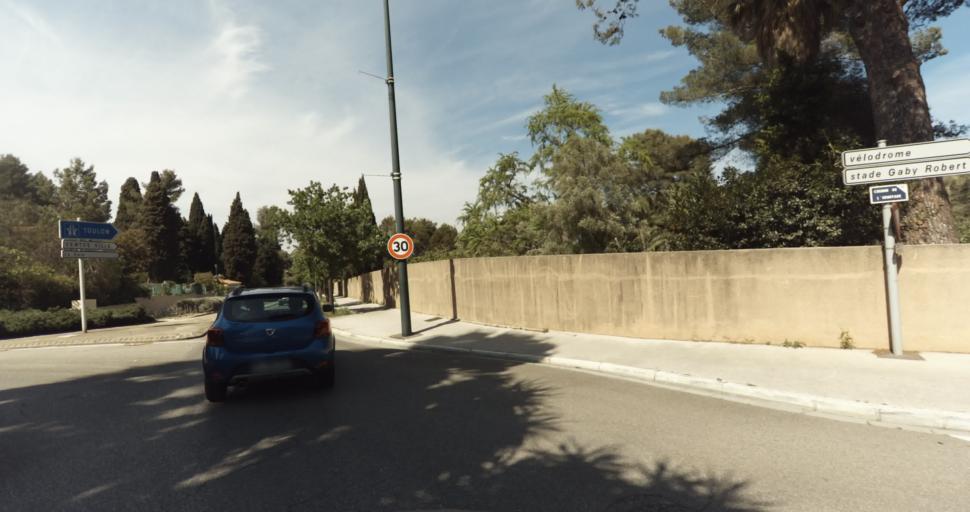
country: FR
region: Provence-Alpes-Cote d'Azur
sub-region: Departement du Var
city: Hyeres
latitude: 43.1031
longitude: 6.1215
